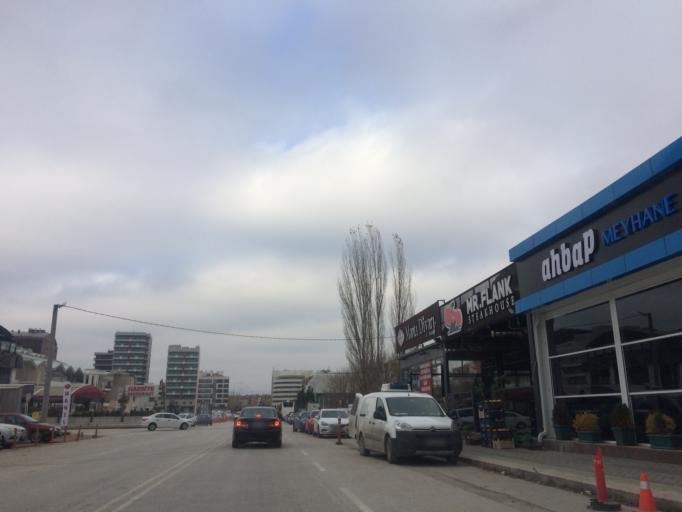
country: TR
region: Eskisehir
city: Eskisehir
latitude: 39.7820
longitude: 30.4991
